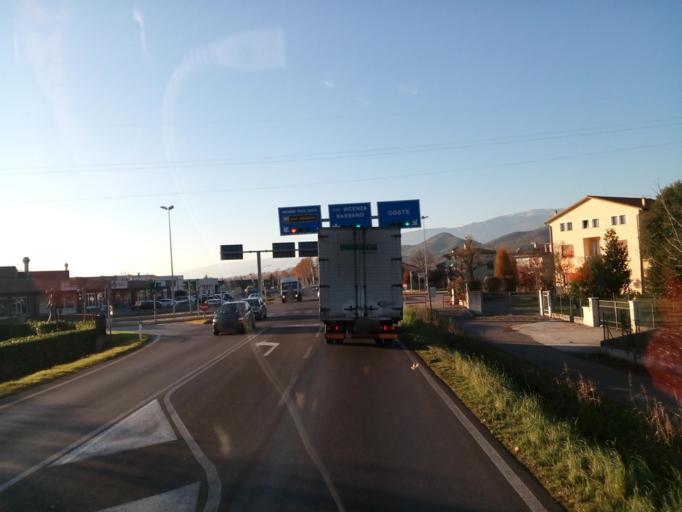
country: IT
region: Veneto
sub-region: Provincia di Treviso
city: Maser
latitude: 45.7940
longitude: 11.9667
